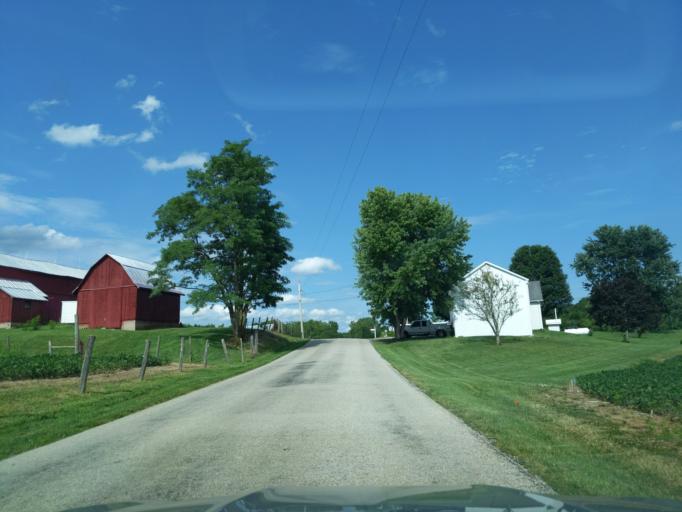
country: US
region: Indiana
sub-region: Ripley County
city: Sunman
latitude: 39.2881
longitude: -85.0980
